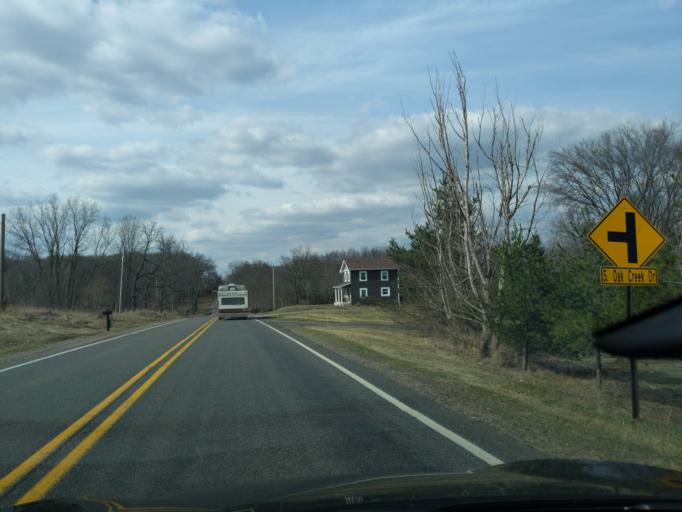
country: US
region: Michigan
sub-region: Ingham County
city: Leslie
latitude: 42.3528
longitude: -84.4169
